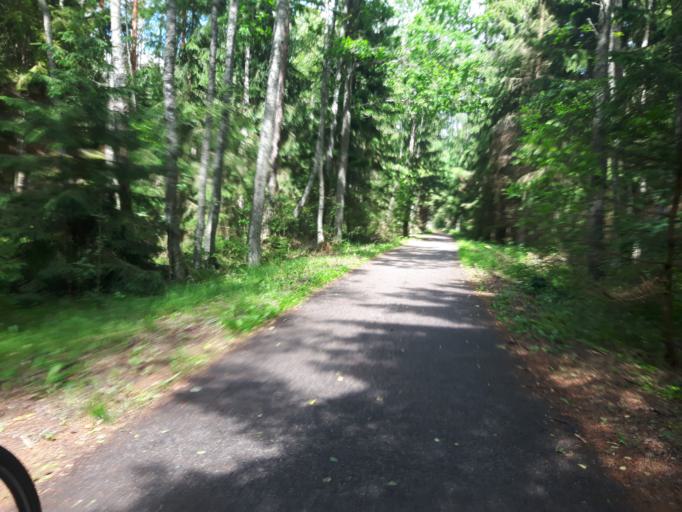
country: LT
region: Klaipedos apskritis
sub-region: Klaipeda
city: Klaipeda
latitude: 55.7869
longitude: 21.0808
